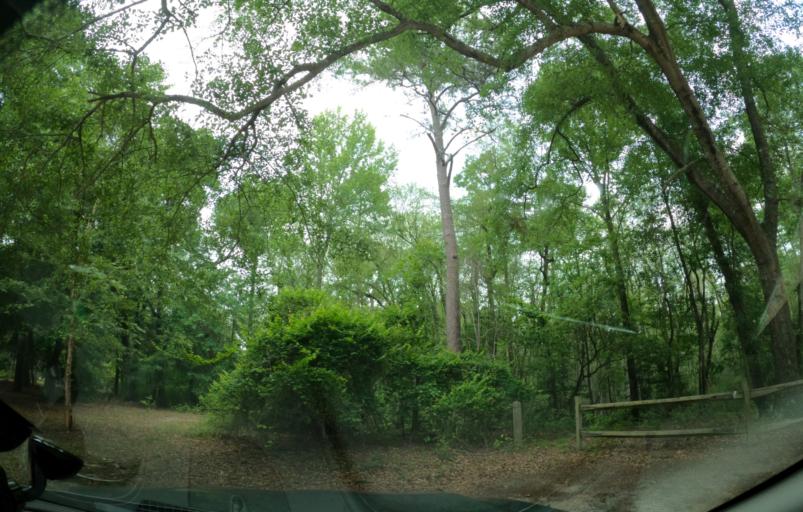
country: US
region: South Carolina
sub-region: Barnwell County
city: Williston
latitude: 33.5508
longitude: -81.4822
